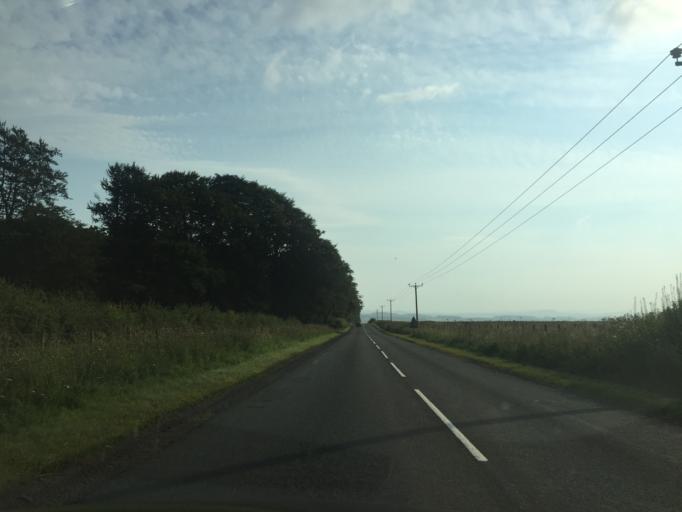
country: GB
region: Scotland
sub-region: The Scottish Borders
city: Kelso
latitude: 55.7182
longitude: -2.4571
